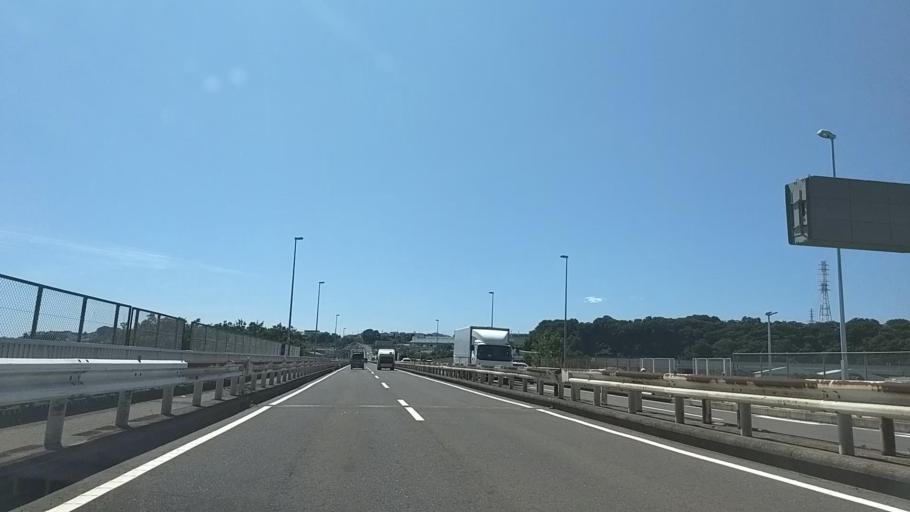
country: JP
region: Kanagawa
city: Zama
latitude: 35.5251
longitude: 139.3616
